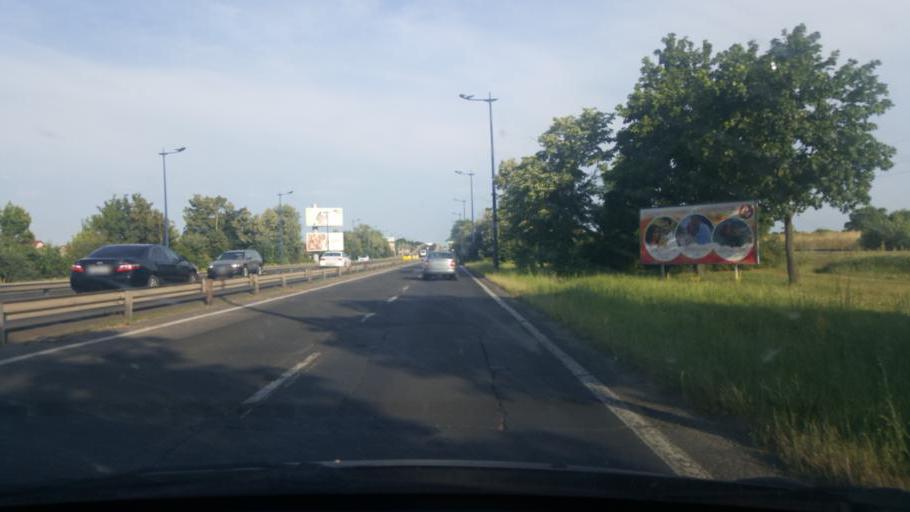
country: HU
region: Budapest
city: Budapest XVIII. keruelet
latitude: 47.4473
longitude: 19.2076
